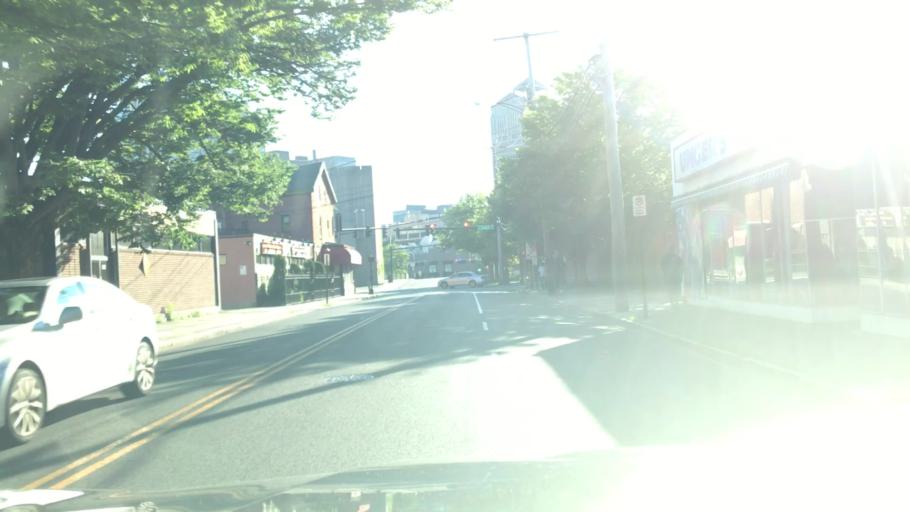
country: US
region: Connecticut
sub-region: New Haven County
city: New Haven
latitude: 41.3076
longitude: -72.9183
